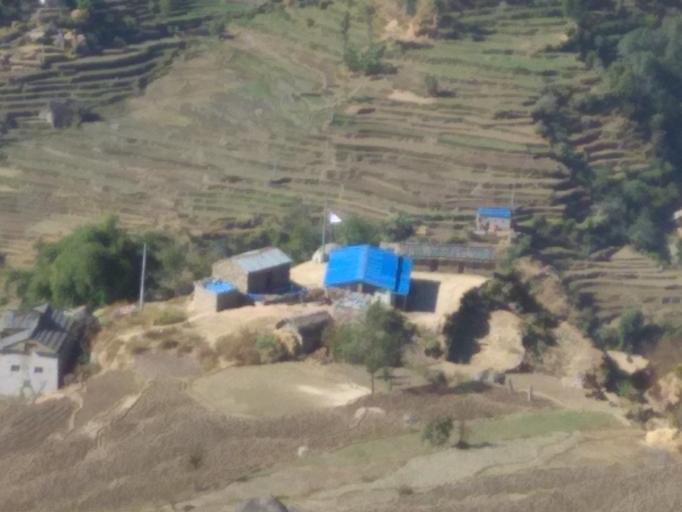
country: NP
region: Far Western
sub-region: Seti Zone
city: Achham
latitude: 29.2606
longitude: 81.6100
